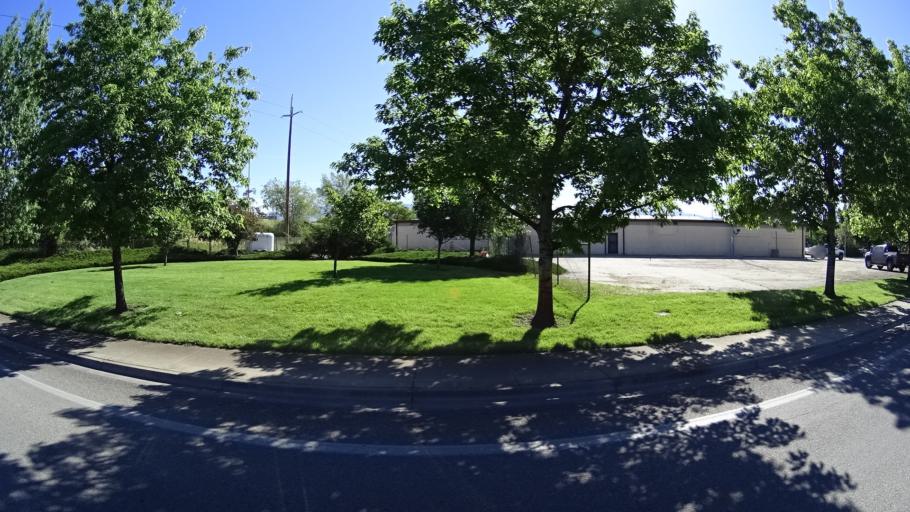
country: US
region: Idaho
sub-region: Ada County
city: Garden City
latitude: 43.6184
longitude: -116.2236
